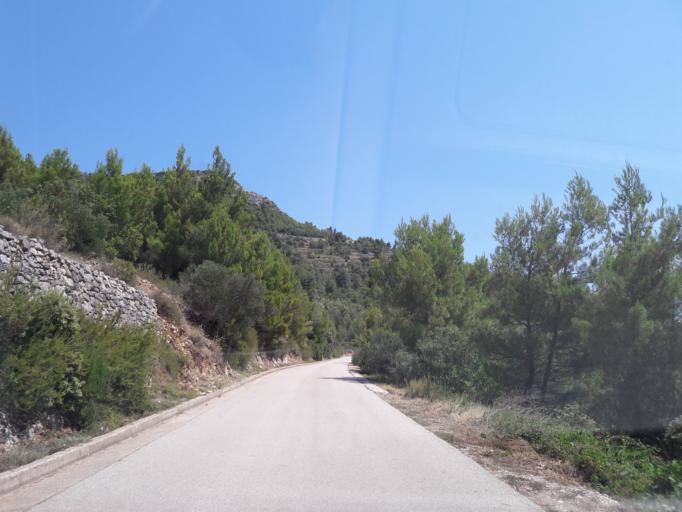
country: HR
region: Dubrovacko-Neretvanska
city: Blato
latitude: 42.9114
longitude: 17.4207
